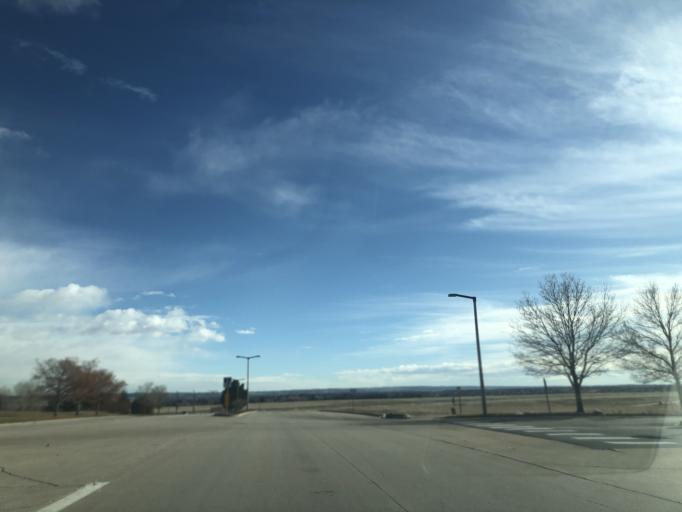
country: US
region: Colorado
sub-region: Douglas County
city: Meridian
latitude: 39.5474
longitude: -104.8431
